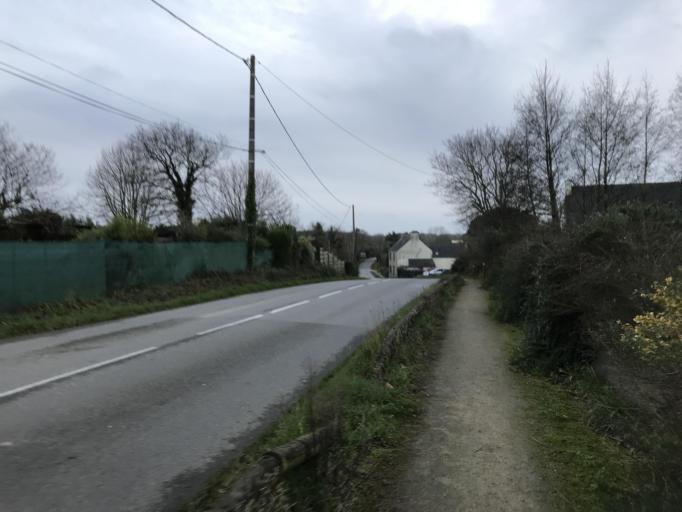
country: FR
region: Brittany
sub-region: Departement du Finistere
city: Loperhet
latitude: 48.3612
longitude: -4.3122
